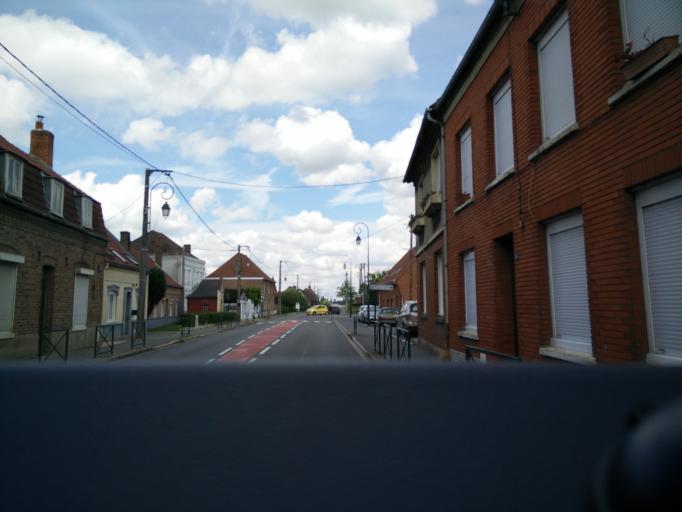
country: FR
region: Nord-Pas-de-Calais
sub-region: Departement du Pas-de-Calais
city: Robecq
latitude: 50.5959
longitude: 2.5630
